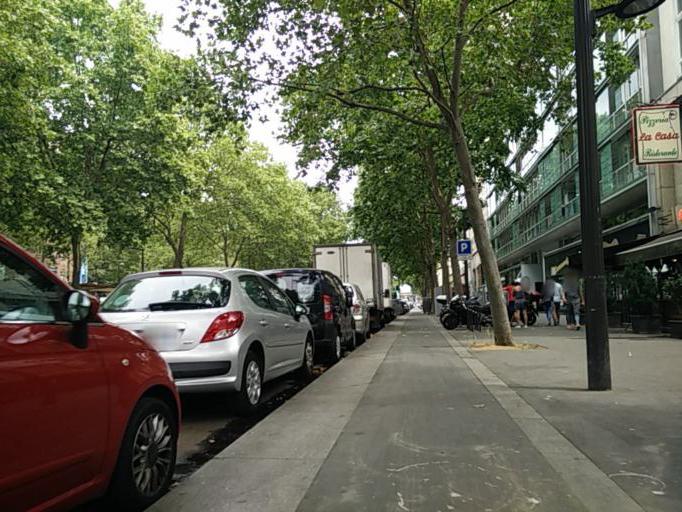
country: FR
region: Ile-de-France
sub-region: Departement de Seine-Saint-Denis
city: Le Pre-Saint-Gervais
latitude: 48.8880
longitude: 2.3896
